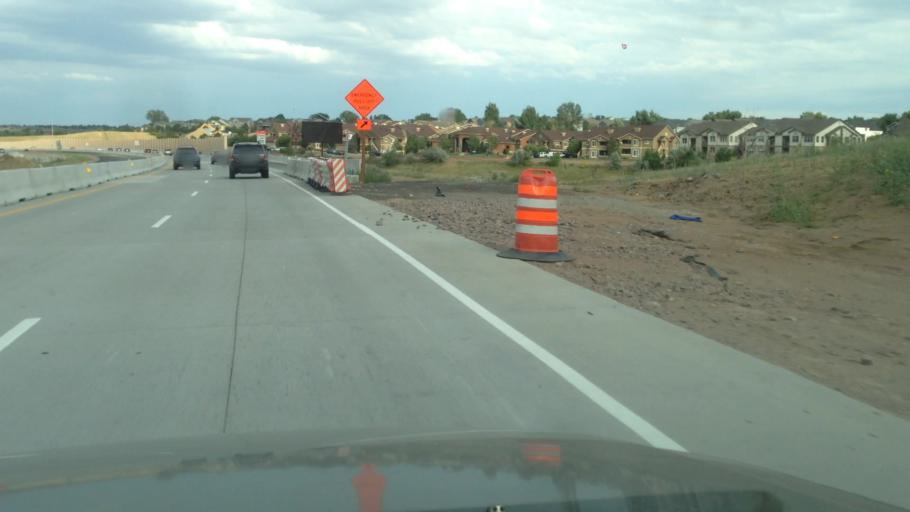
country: US
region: Colorado
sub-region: Arapahoe County
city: Southglenn
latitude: 39.5603
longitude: -104.9396
